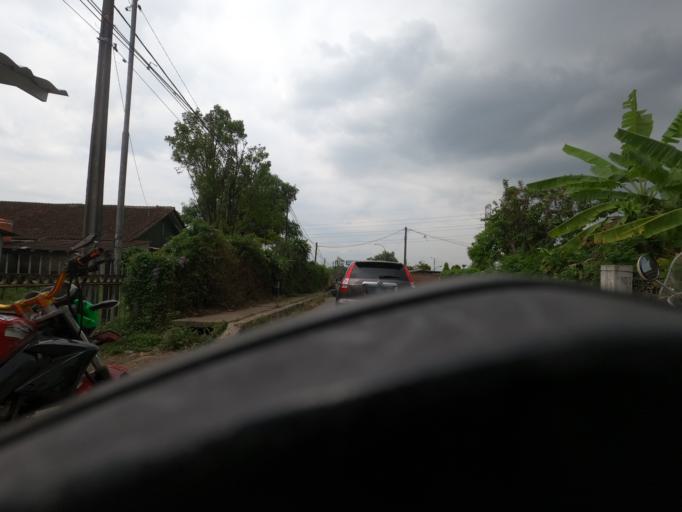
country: ID
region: West Java
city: Padalarang
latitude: -6.8431
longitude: 107.4947
